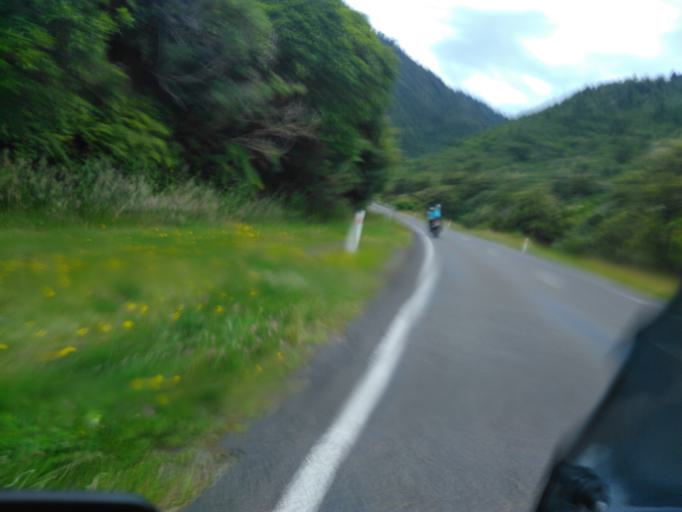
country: NZ
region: Bay of Plenty
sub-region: Opotiki District
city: Opotiki
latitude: -38.2913
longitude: 177.3828
